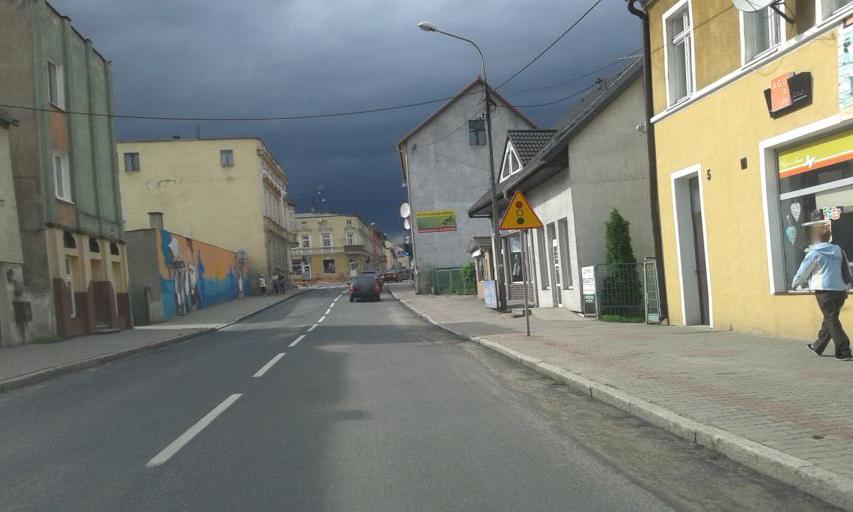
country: PL
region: Greater Poland Voivodeship
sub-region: Powiat zlotowski
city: Jastrowie
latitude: 53.4198
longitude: 16.8161
